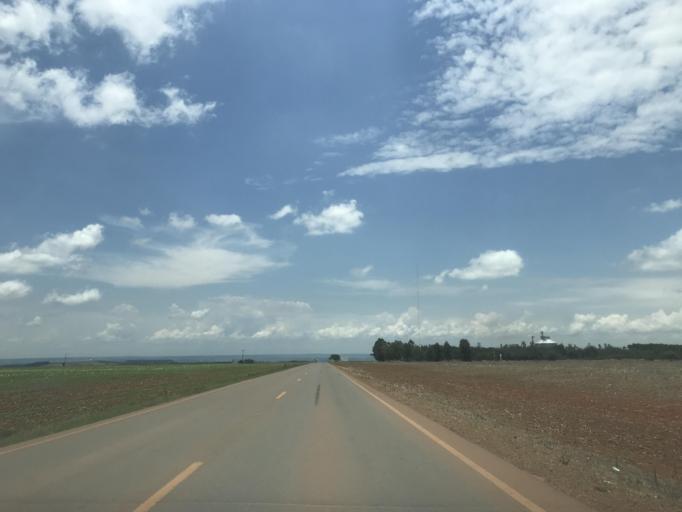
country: BR
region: Goias
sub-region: Vianopolis
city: Vianopolis
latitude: -16.5421
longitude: -48.2600
